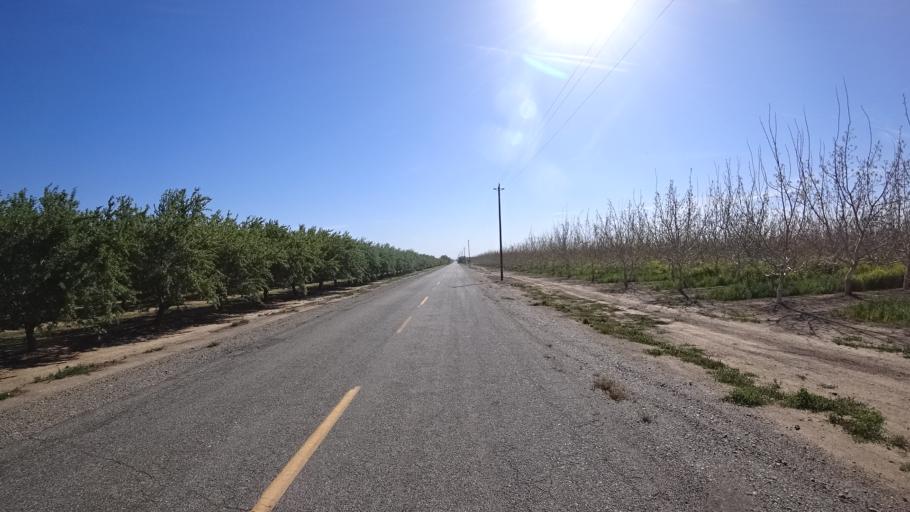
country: US
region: California
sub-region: Glenn County
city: Willows
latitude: 39.6113
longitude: -122.1804
